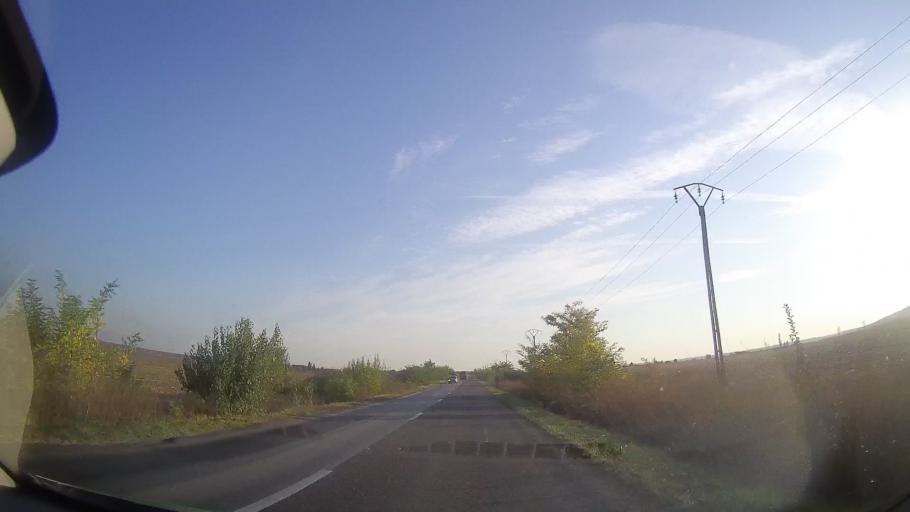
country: RO
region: Timis
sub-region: Comuna Pischia
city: Pischia
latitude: 45.8851
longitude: 21.3441
